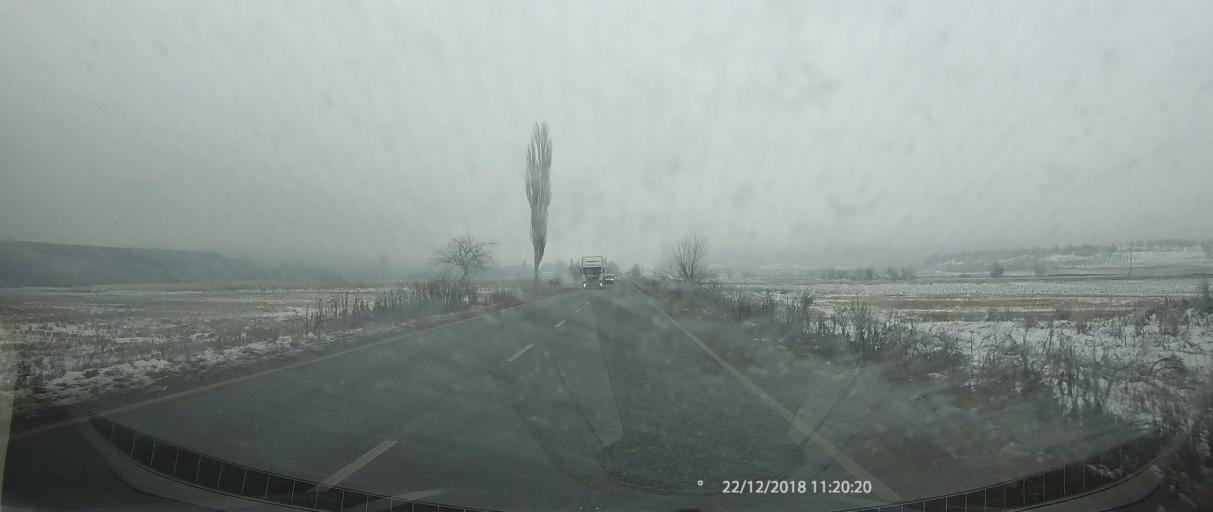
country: BG
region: Kyustendil
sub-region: Obshtina Kyustendil
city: Kyustendil
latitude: 42.2653
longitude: 22.8139
